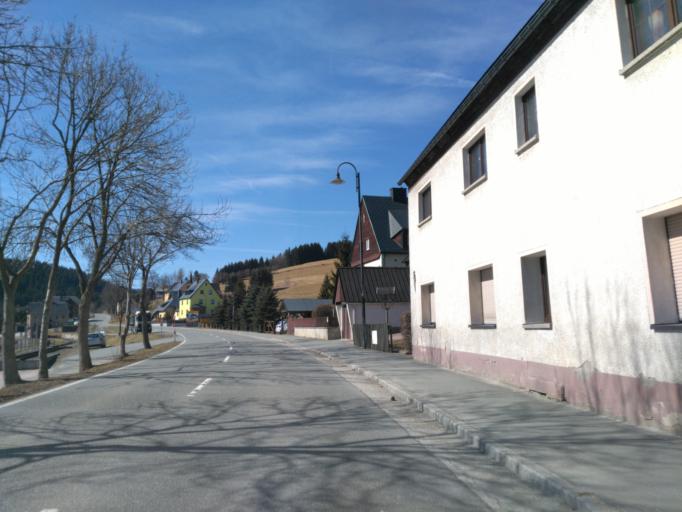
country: CZ
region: Ustecky
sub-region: Okres Chomutov
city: Kovarska
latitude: 50.4423
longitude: 13.0097
